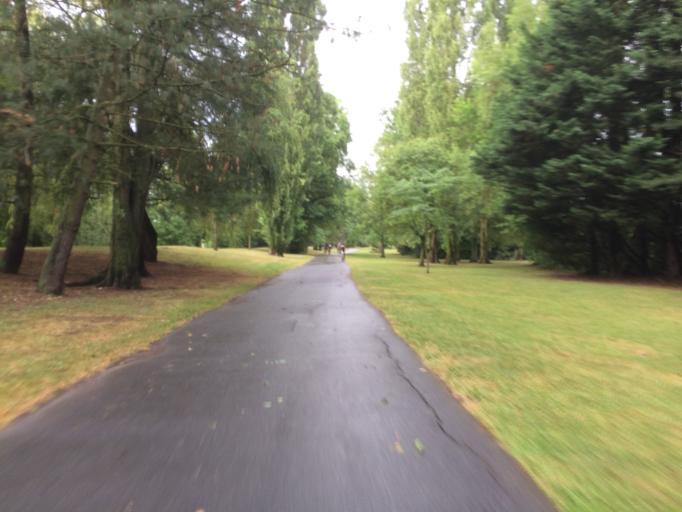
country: FR
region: Picardie
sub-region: Departement de l'Oise
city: Venette
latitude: 49.4016
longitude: 2.7937
